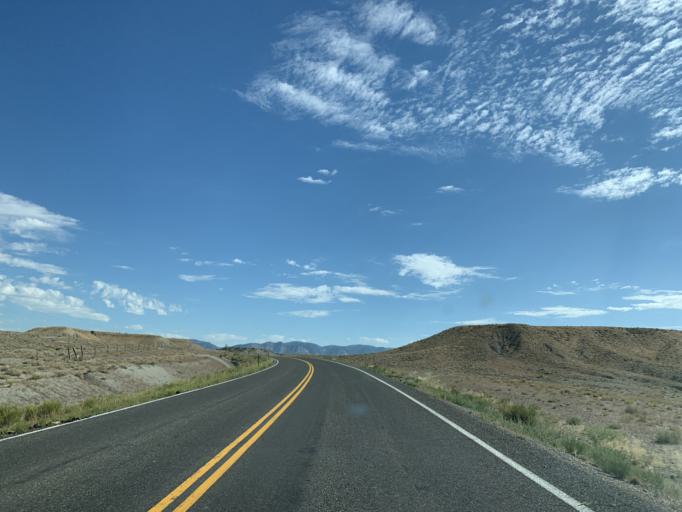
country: US
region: Utah
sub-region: Carbon County
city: Wellington
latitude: 39.5553
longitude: -110.6669
